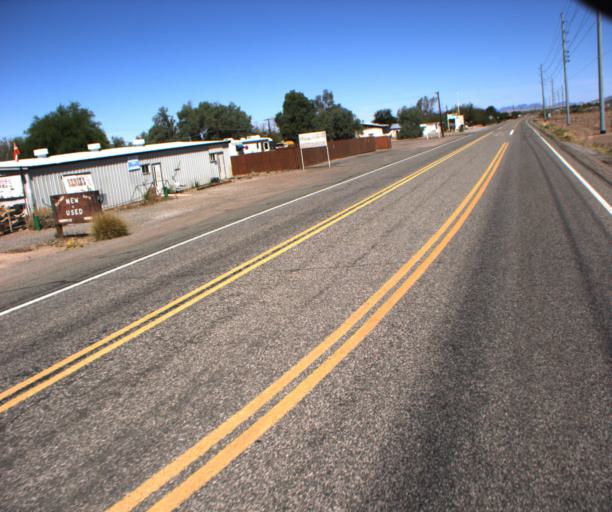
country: US
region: Arizona
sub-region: La Paz County
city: Cienega Springs
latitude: 33.9339
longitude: -114.0070
